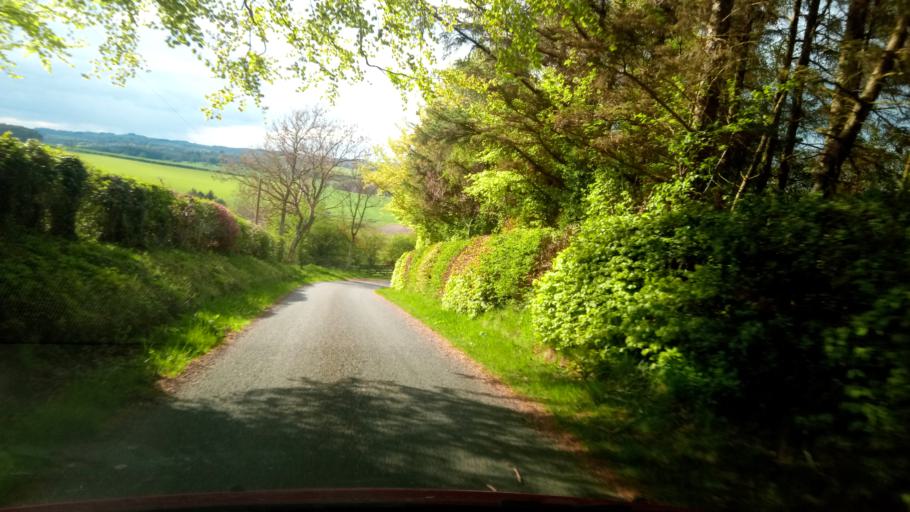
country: GB
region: Scotland
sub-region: The Scottish Borders
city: Saint Boswells
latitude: 55.5156
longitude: -2.6772
